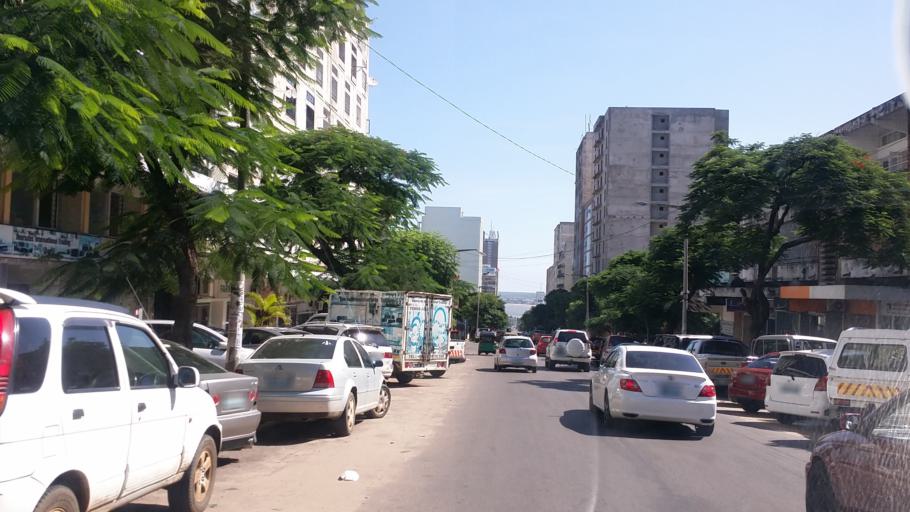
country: MZ
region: Maputo City
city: Maputo
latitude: -25.9663
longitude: 32.5791
